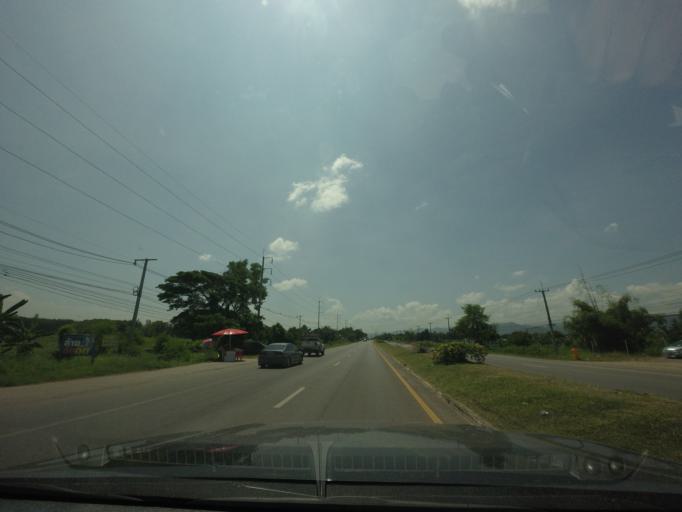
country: TH
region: Phetchabun
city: Lom Sak
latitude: 16.7155
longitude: 101.1807
